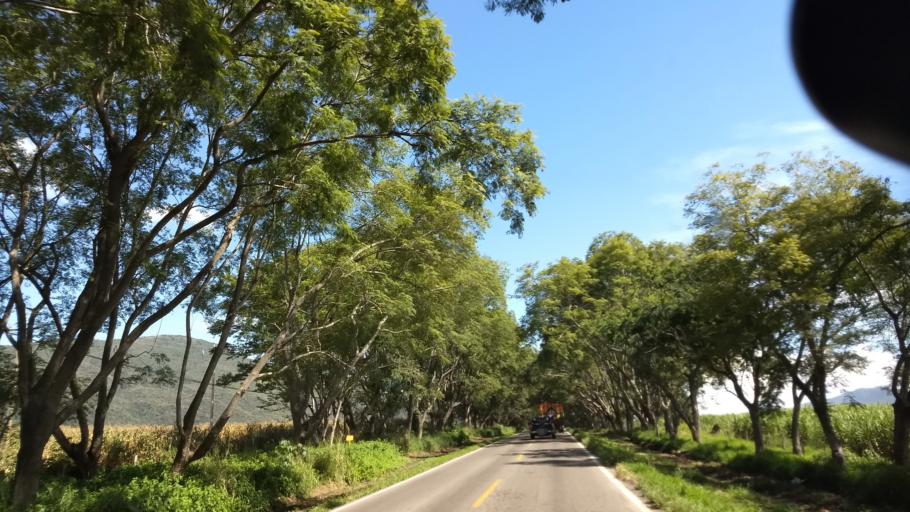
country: MX
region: Jalisco
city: Tuxpan
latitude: 19.5320
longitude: -103.4184
